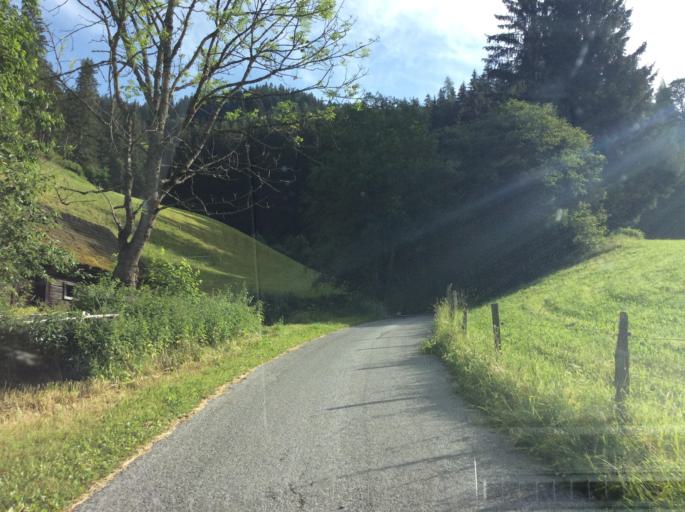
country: AT
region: Salzburg
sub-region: Politischer Bezirk Sankt Johann im Pongau
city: Forstau
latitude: 47.4052
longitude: 13.5843
